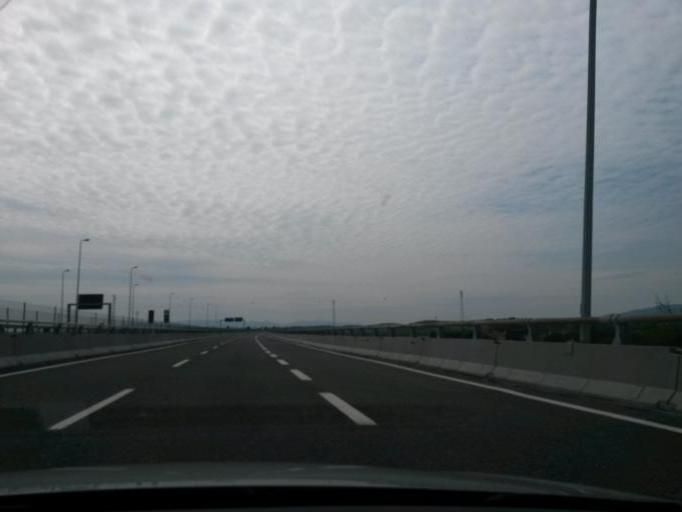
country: IT
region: Tuscany
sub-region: Provincia di Livorno
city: Vicarello
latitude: 43.6127
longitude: 10.4404
